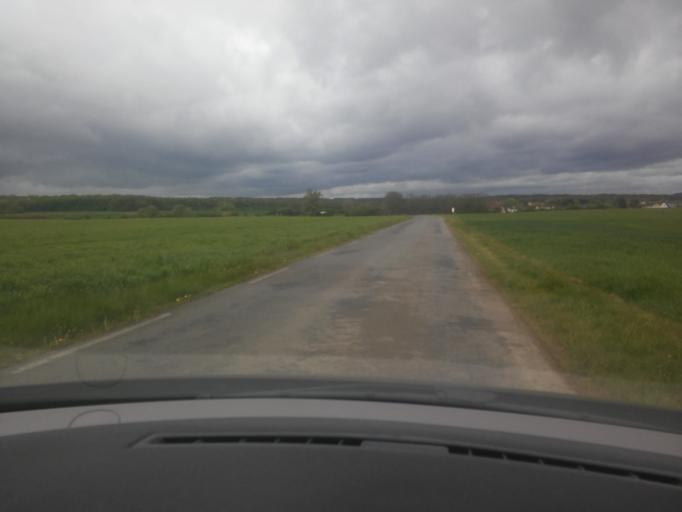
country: FR
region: Lorraine
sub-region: Departement de la Moselle
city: Mecleuves
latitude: 49.0514
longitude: 6.2516
